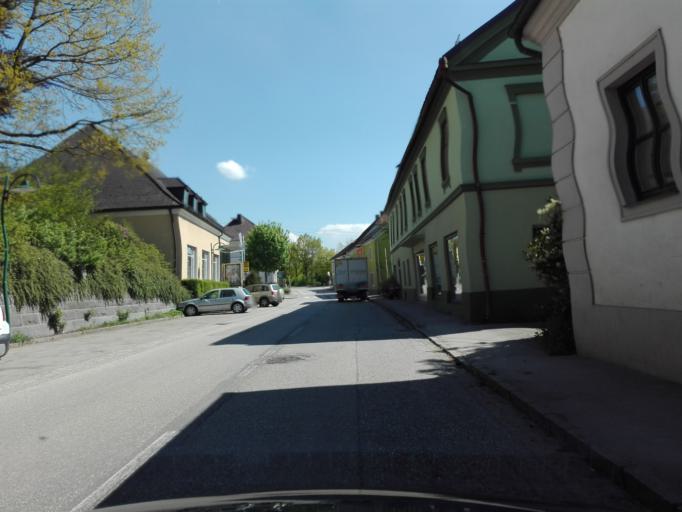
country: AT
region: Upper Austria
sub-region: Politischer Bezirk Grieskirchen
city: Bad Schallerbach
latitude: 48.3149
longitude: 13.9043
